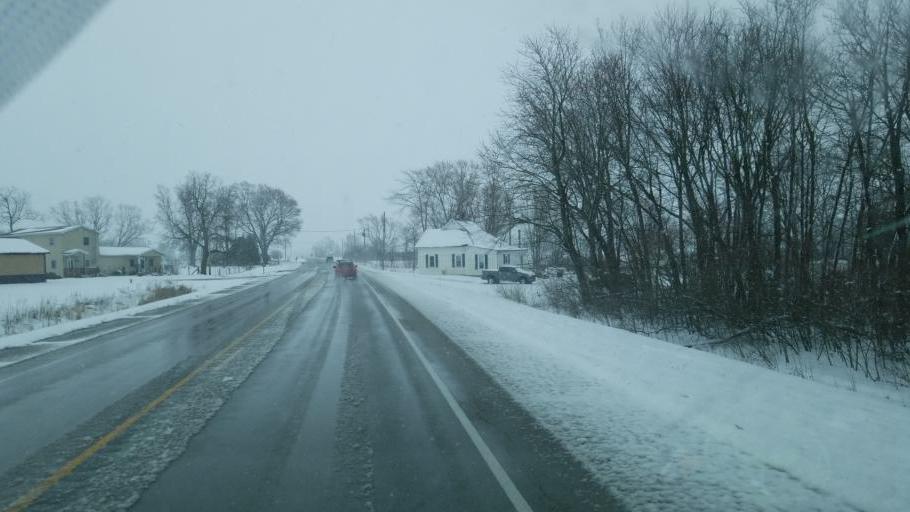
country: US
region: Indiana
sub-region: Randolph County
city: Parker City
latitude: 40.0723
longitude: -85.2709
